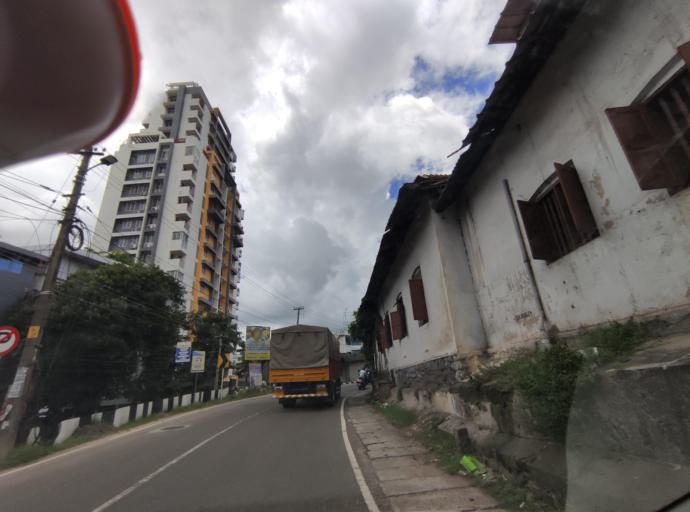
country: IN
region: Kerala
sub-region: Thiruvananthapuram
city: Thiruvananthapuram
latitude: 8.5137
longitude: 76.9467
